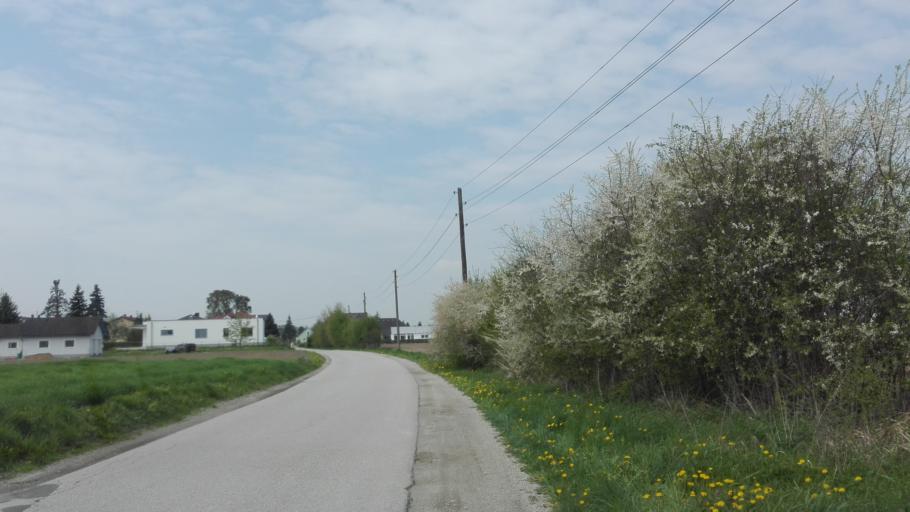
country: AT
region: Upper Austria
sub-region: Politischer Bezirk Perg
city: Perg
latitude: 48.2295
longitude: 14.5885
